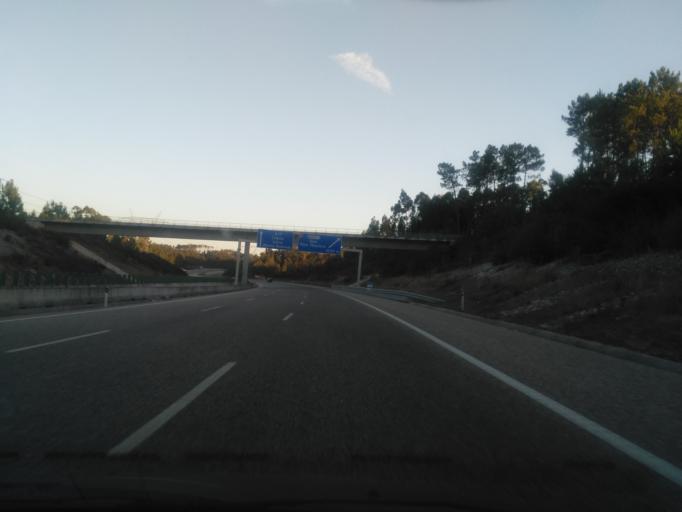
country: PT
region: Leiria
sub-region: Pombal
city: Lourical
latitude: 39.9572
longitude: -8.7746
